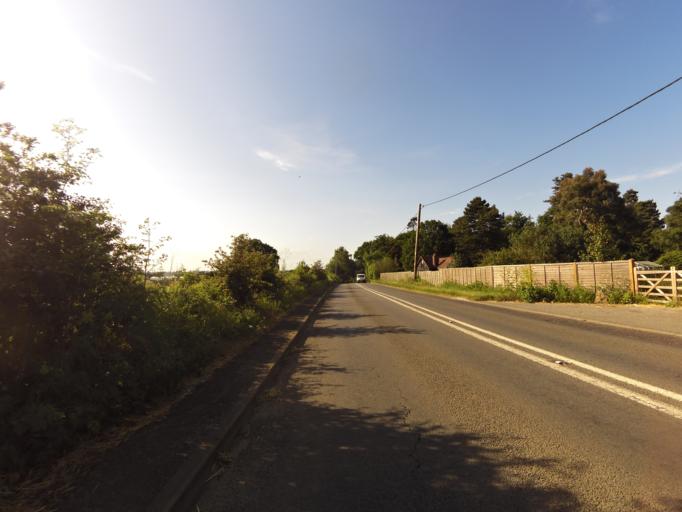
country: GB
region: England
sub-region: Suffolk
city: Woodbridge
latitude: 52.0973
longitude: 1.3486
